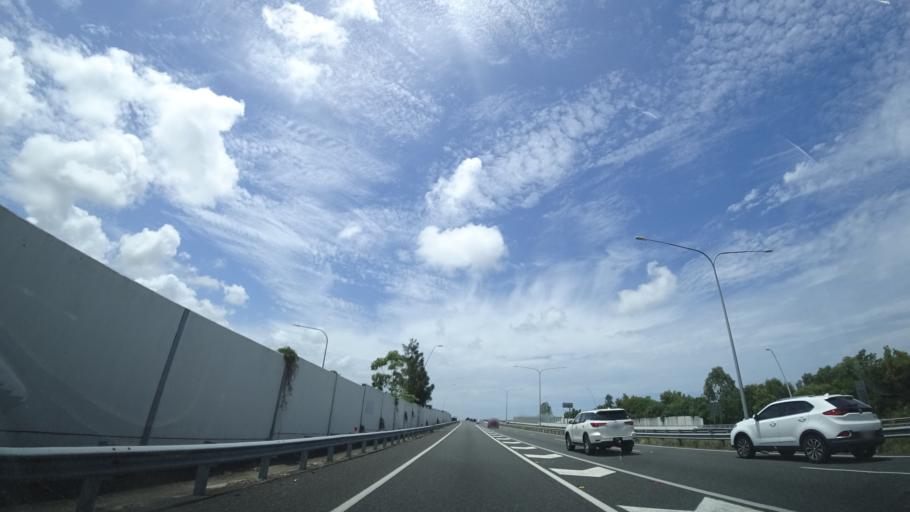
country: AU
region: Queensland
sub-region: Sunshine Coast
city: Buderim
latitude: -26.6448
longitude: 153.0670
